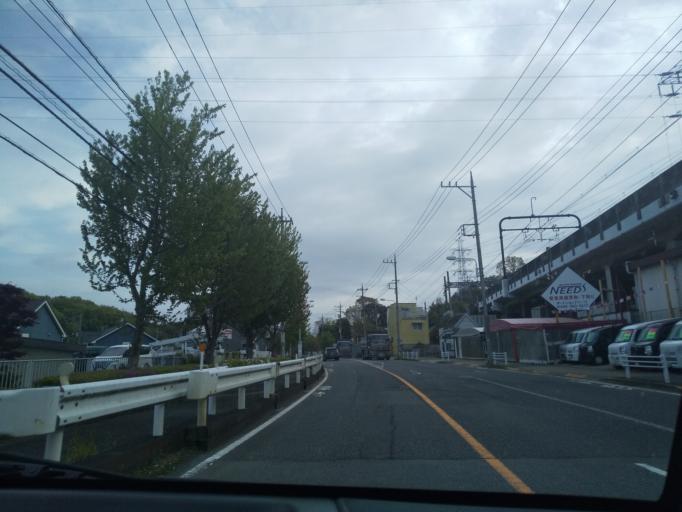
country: JP
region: Tokyo
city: Chofugaoka
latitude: 35.6285
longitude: 139.4901
